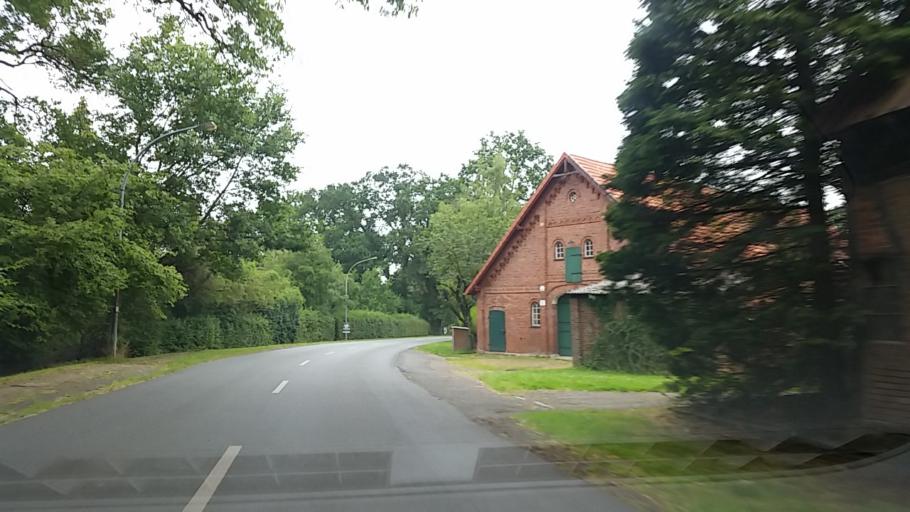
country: DE
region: Lower Saxony
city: Vollersode
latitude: 53.4134
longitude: 8.9143
